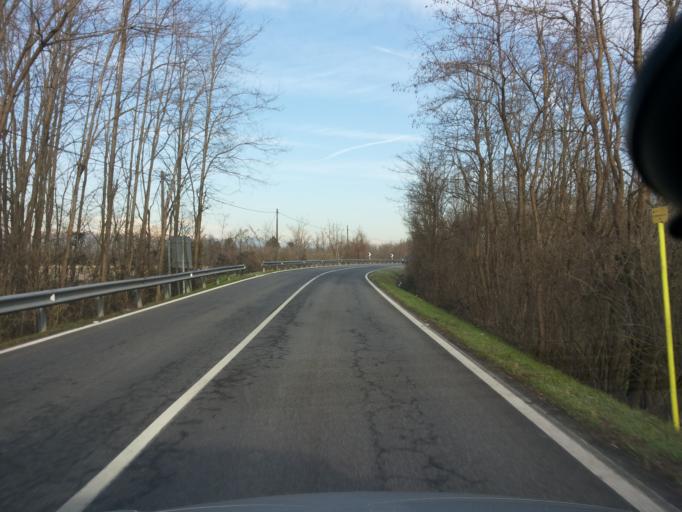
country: IT
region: Piedmont
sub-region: Provincia di Vercelli
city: Quinto Vercellese
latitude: 45.3781
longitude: 8.3725
